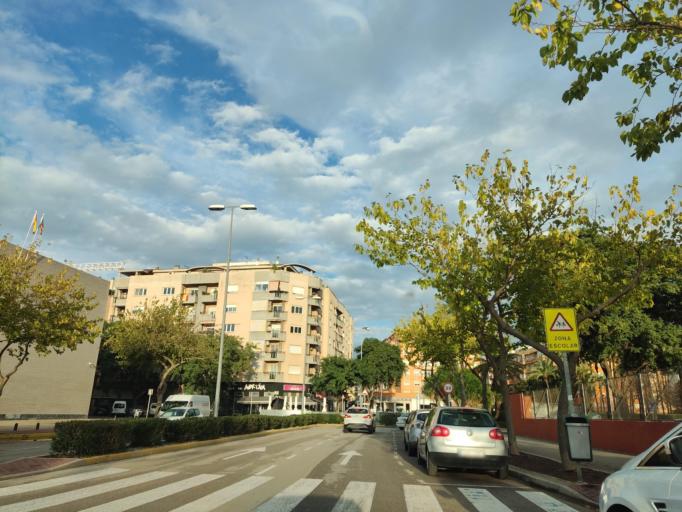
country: ES
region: Valencia
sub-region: Provincia de Alicante
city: Denia
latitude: 38.8355
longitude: 0.1016
